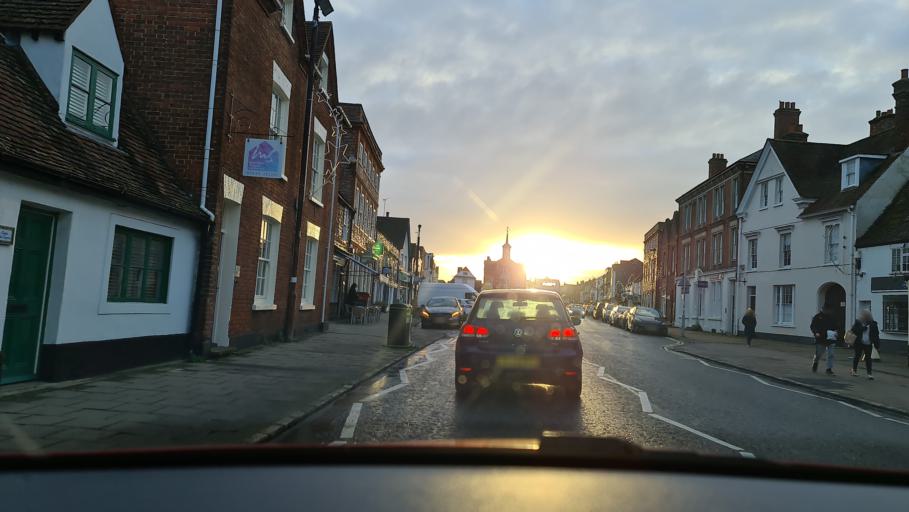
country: GB
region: England
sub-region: Oxfordshire
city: Thame
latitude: 51.7488
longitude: -0.9803
